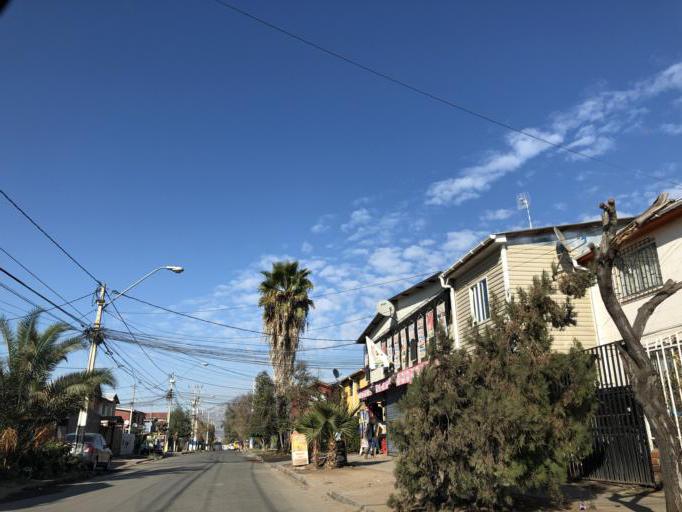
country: CL
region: Santiago Metropolitan
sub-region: Provincia de Cordillera
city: Puente Alto
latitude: -33.6192
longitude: -70.6152
